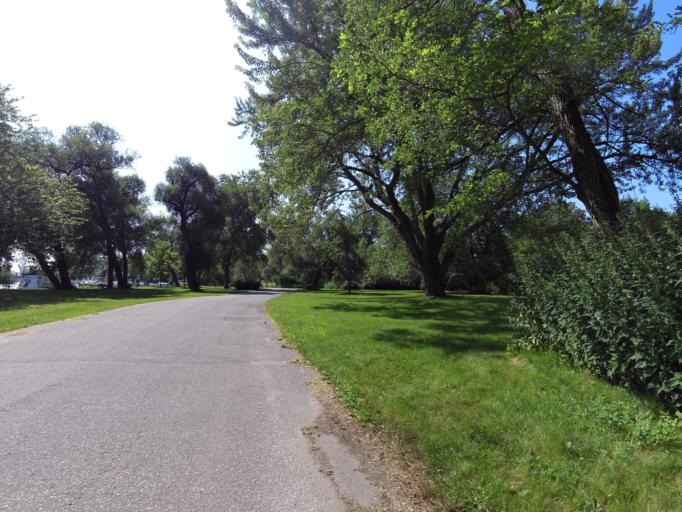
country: CA
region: Ontario
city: Toronto
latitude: 43.6184
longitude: -79.3909
